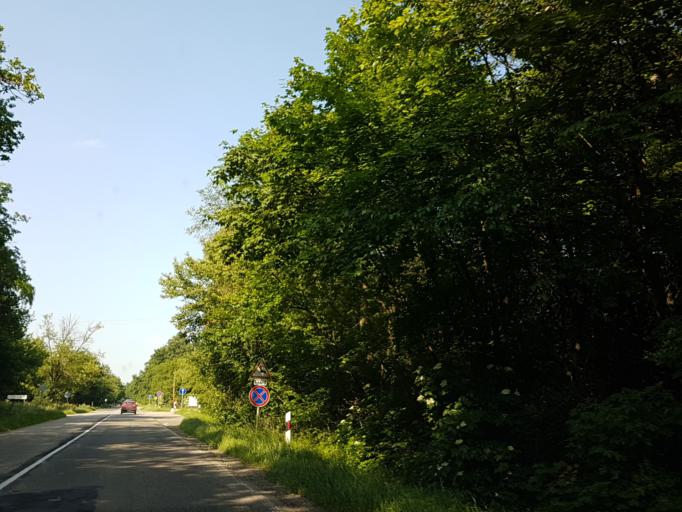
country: HU
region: Fejer
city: Polgardi
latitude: 47.0223
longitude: 18.2820
